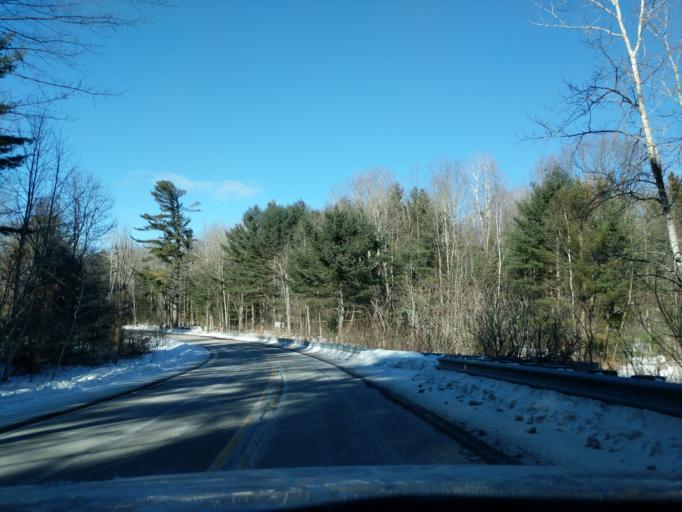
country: US
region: Wisconsin
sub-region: Menominee County
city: Keshena
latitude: 45.1029
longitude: -88.6346
